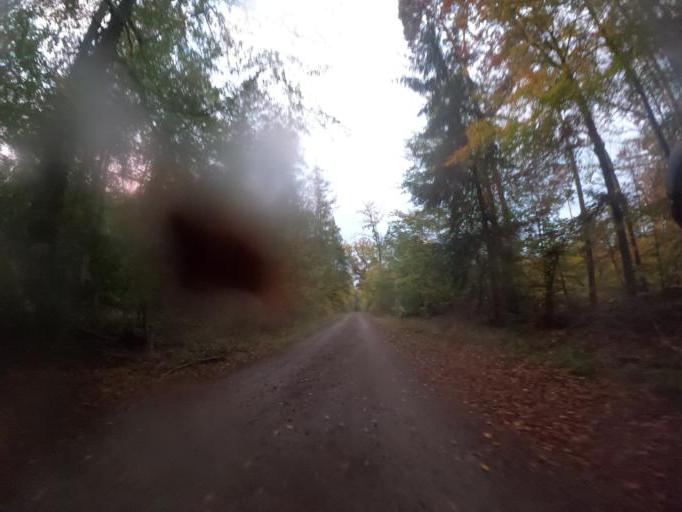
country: DE
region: Hesse
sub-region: Regierungsbezirk Darmstadt
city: Neu Isenburg
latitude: 50.0573
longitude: 8.7324
